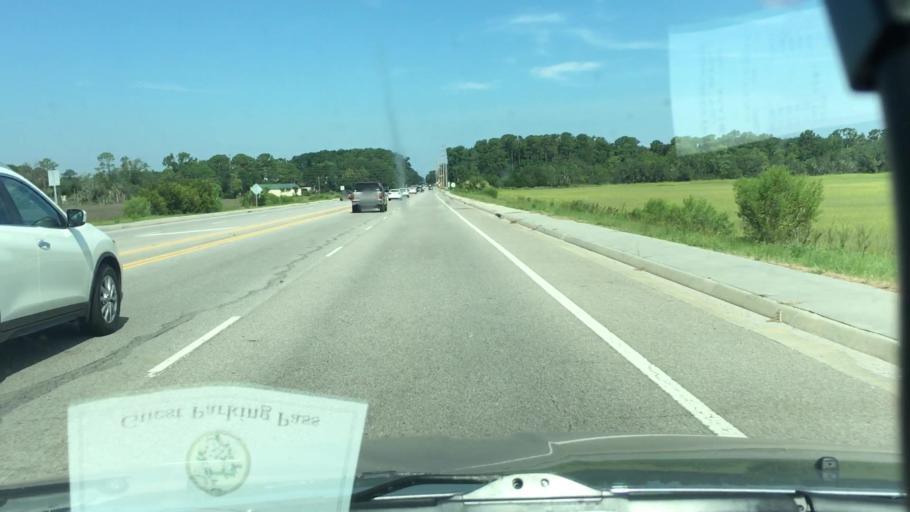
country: US
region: South Carolina
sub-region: Beaufort County
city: Beaufort
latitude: 32.4088
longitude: -80.6402
